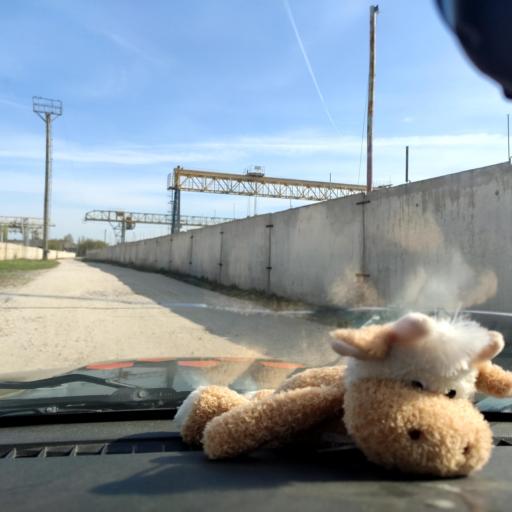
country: RU
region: Samara
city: Tol'yatti
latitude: 53.5731
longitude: 49.2749
